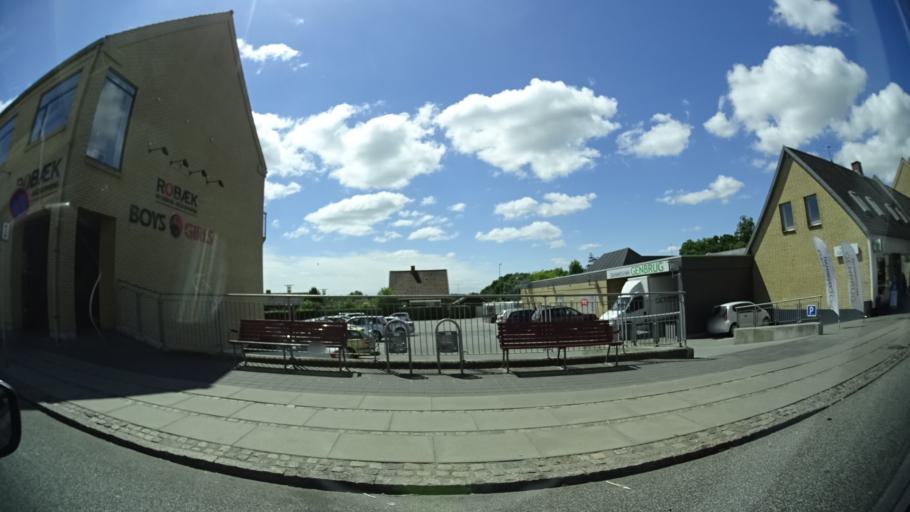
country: DK
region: Central Jutland
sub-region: Syddjurs Kommune
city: Ronde
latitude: 56.3006
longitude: 10.4765
